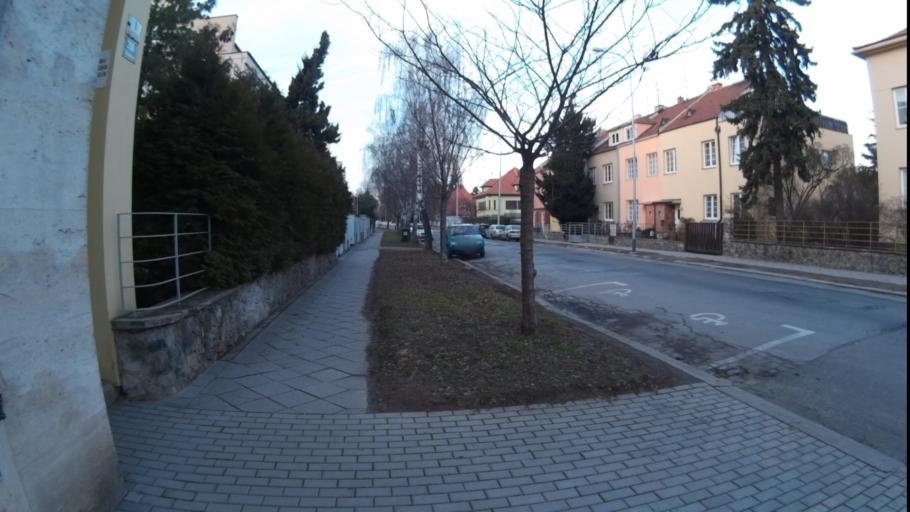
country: CZ
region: South Moravian
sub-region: Mesto Brno
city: Brno
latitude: 49.1955
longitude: 16.5857
